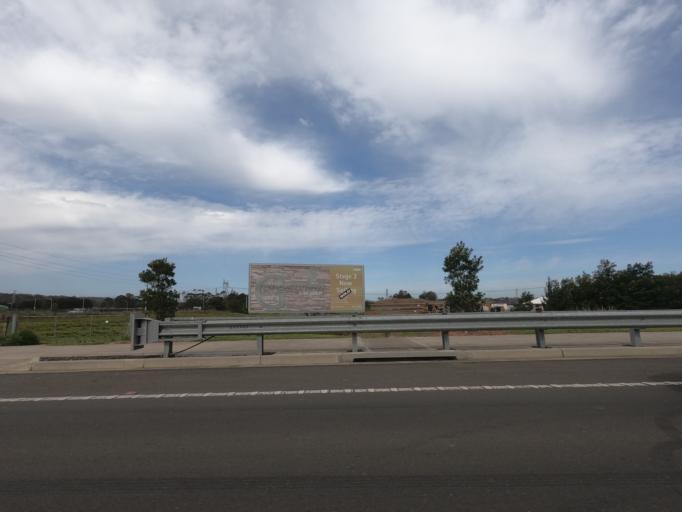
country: AU
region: New South Wales
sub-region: Wollongong
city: Dapto
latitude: -34.4793
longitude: 150.7659
